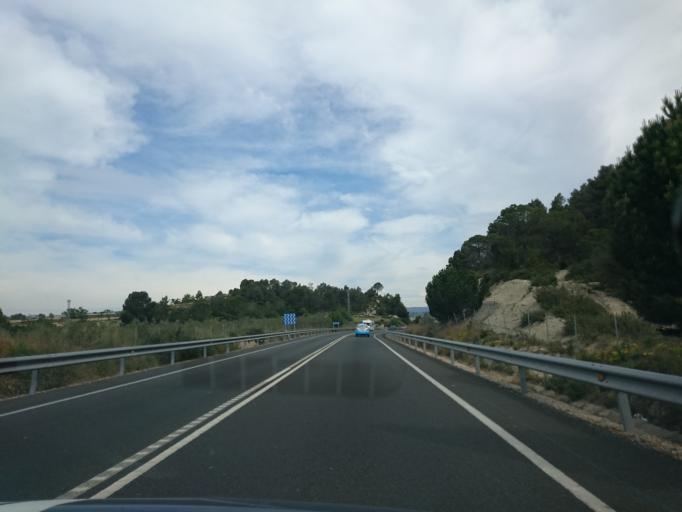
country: ES
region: Catalonia
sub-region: Provincia de Barcelona
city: La Pobla de Claramunt
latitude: 41.5711
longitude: 1.6740
